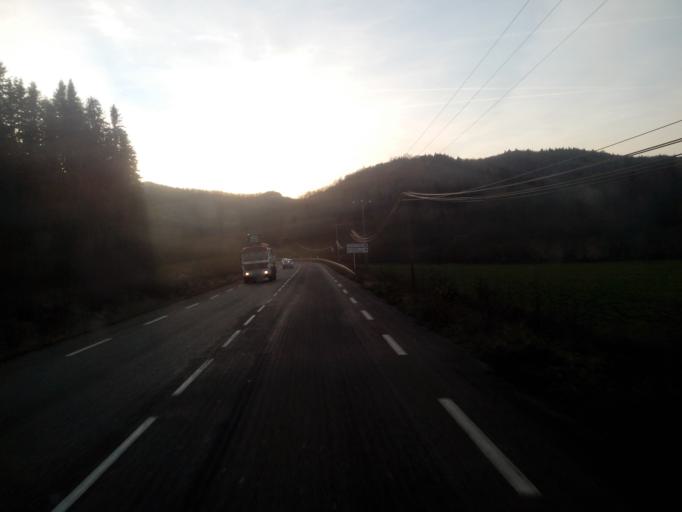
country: FR
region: Midi-Pyrenees
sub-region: Departement de l'Ariege
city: Lavelanet
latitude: 42.9157
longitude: 1.7975
